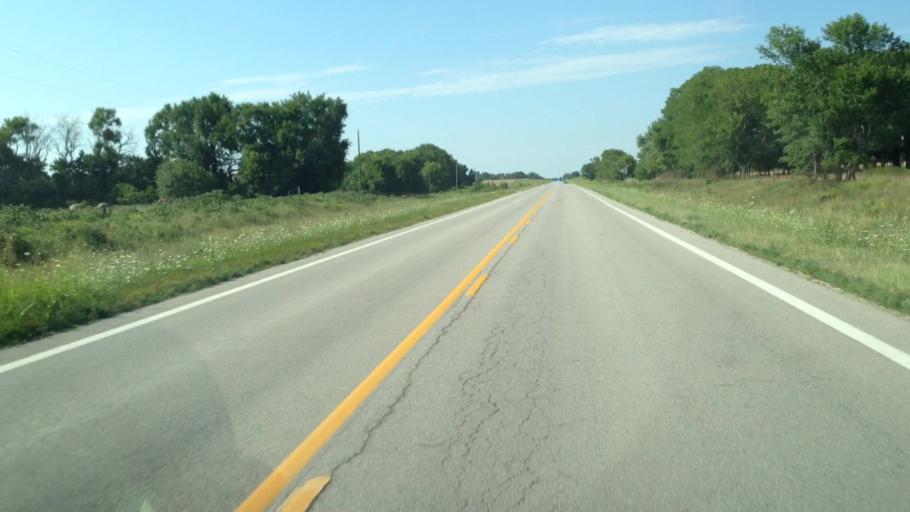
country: US
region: Kansas
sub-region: Neosho County
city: Erie
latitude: 37.7220
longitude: -95.1607
